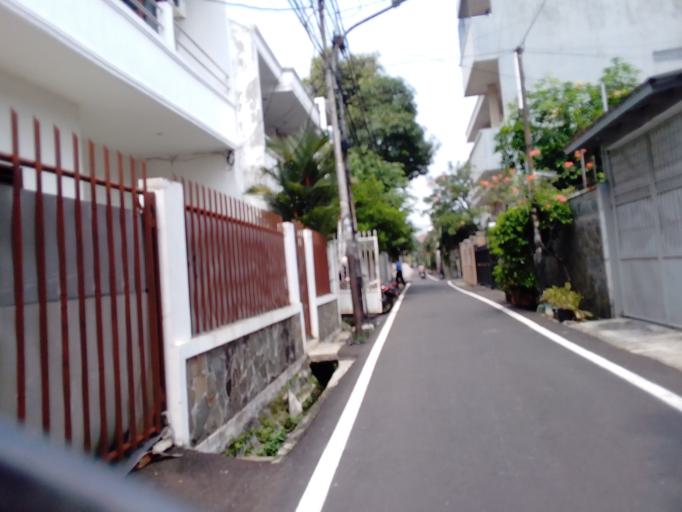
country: ID
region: Jakarta Raya
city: Jakarta
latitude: -6.1731
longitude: 106.8108
